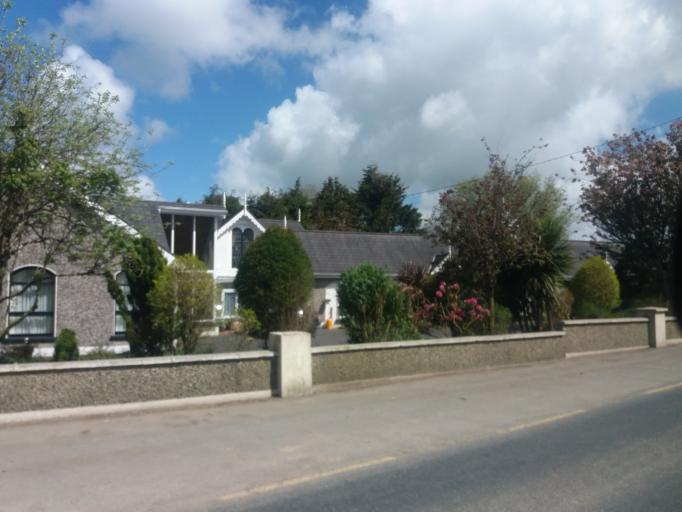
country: IE
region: Leinster
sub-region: Loch Garman
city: Loch Garman
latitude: 52.2833
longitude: -6.6508
